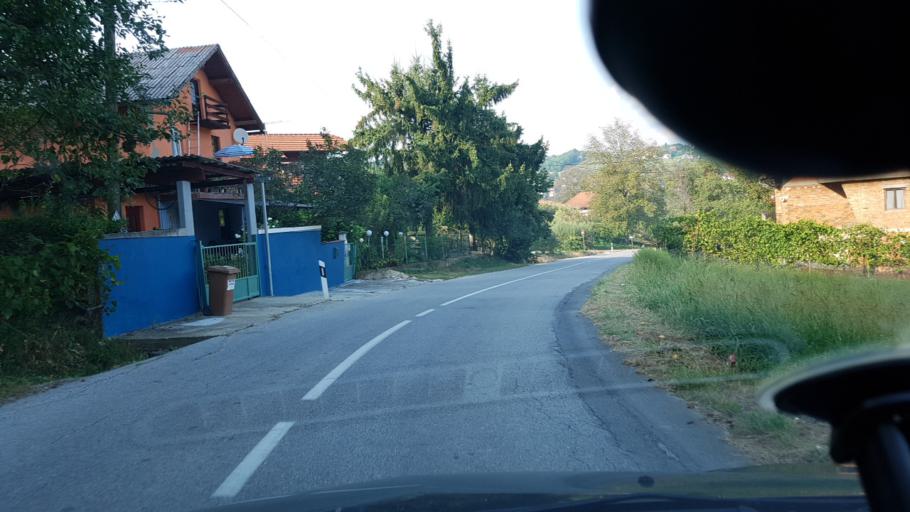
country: HR
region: Krapinsko-Zagorska
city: Pregrada
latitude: 46.0608
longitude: 15.7738
